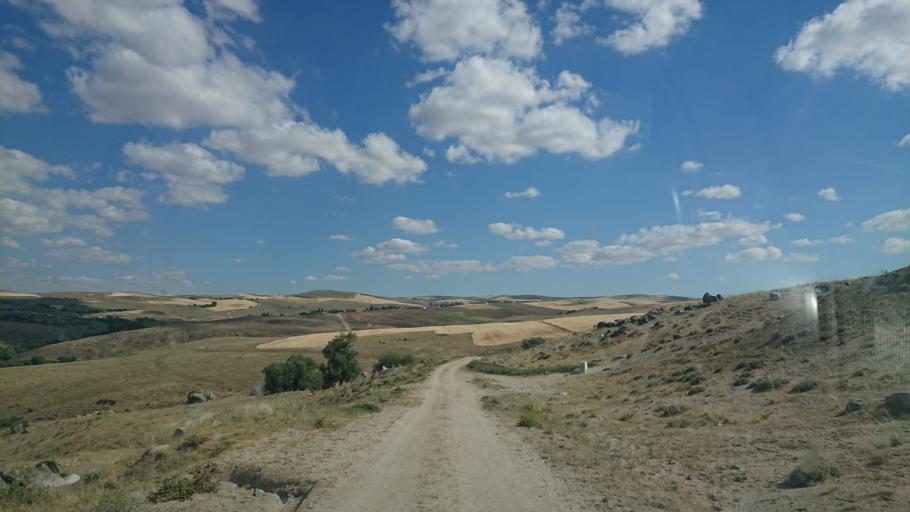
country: TR
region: Aksaray
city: Sariyahsi
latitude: 38.9220
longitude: 33.8524
